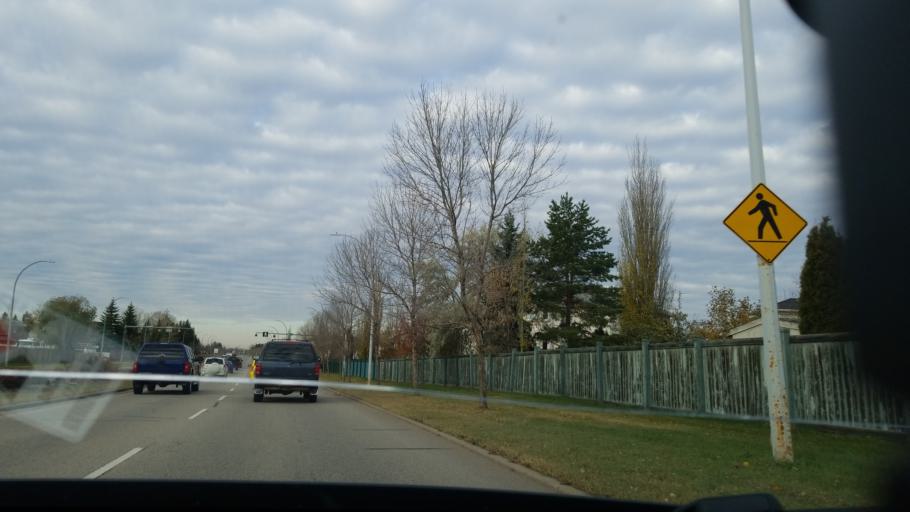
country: CA
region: Alberta
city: Edmonton
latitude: 53.6159
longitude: -113.4742
